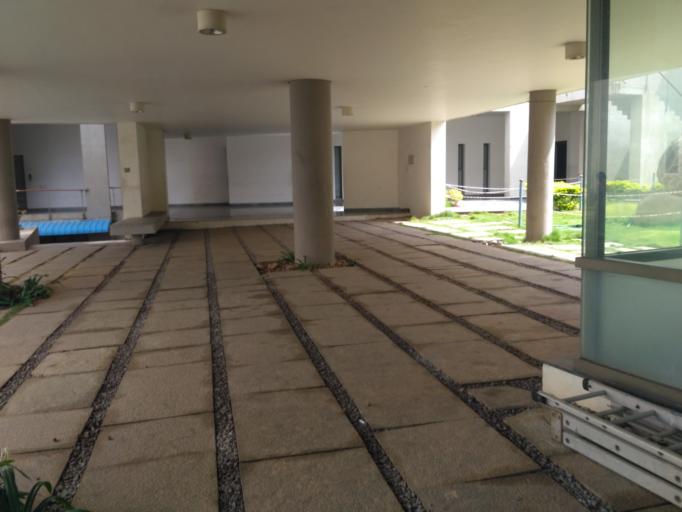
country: IN
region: Telangana
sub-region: Rangareddi
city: Kukatpalli
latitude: 17.4357
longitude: 78.3601
